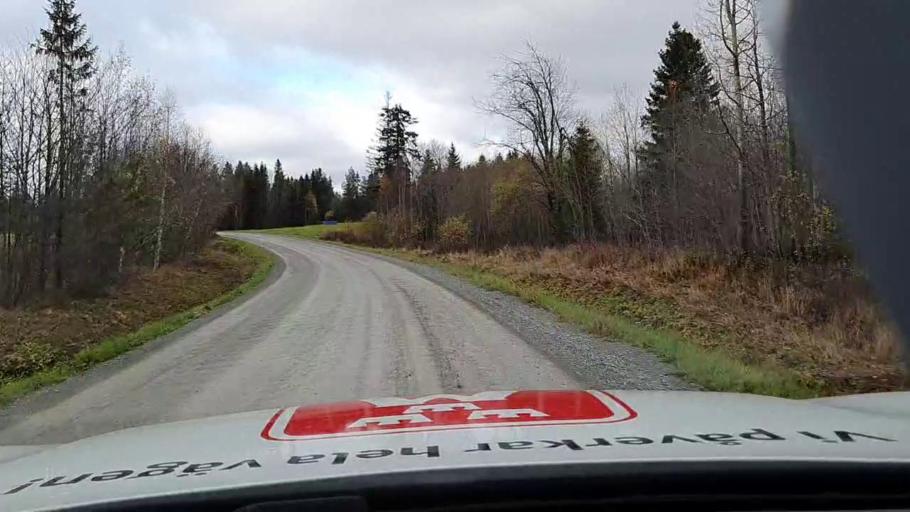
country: SE
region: Jaemtland
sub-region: Bergs Kommun
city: Hoverberg
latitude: 62.9785
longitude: 14.2157
